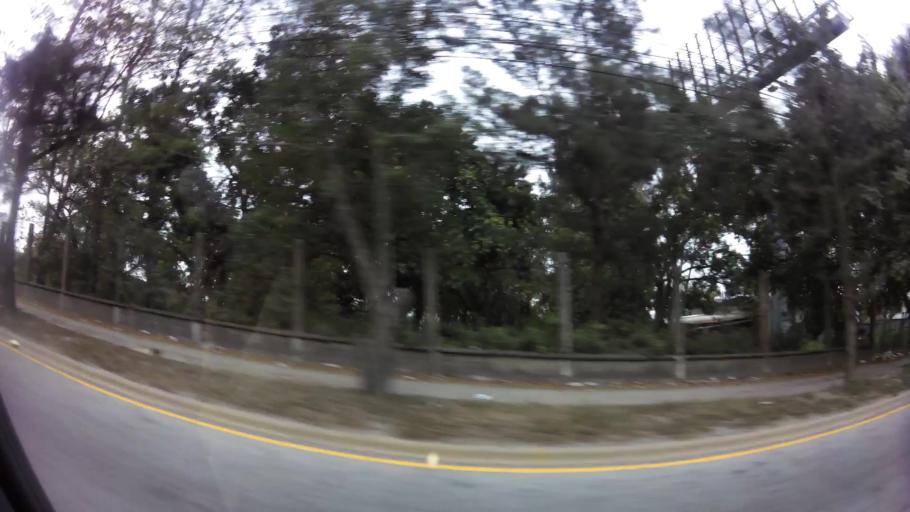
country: HN
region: Cortes
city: Armenta
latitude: 15.4649
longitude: -88.0324
